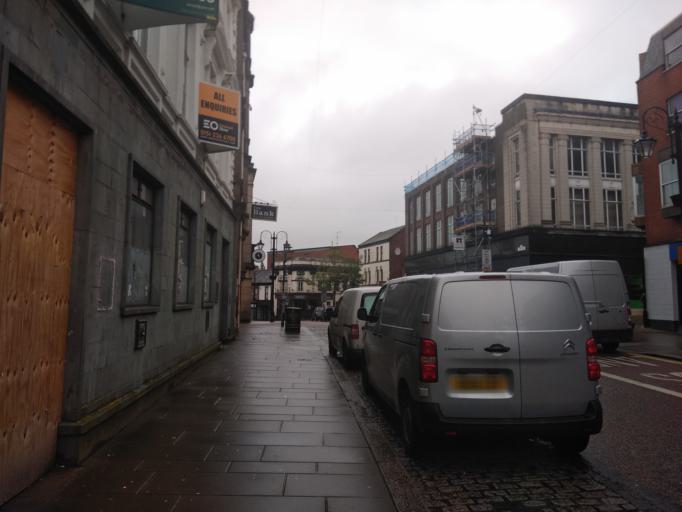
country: GB
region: Wales
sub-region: Wrexham
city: Wrexham
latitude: 53.0451
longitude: -2.9931
